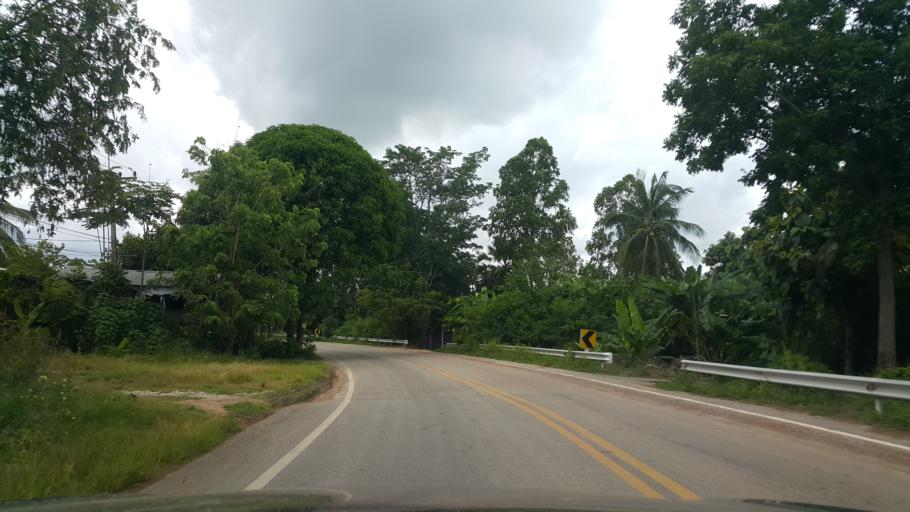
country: TH
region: Sukhothai
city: Sukhothai
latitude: 16.9166
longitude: 99.8737
